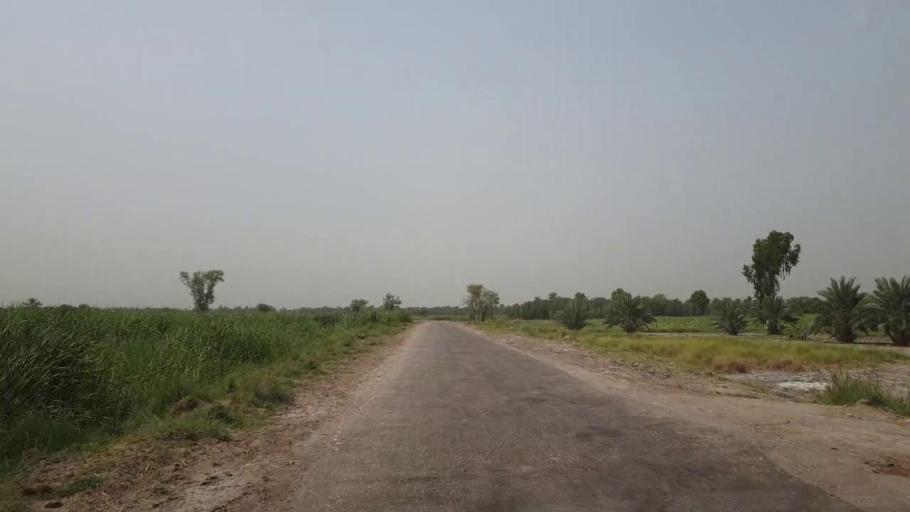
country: PK
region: Sindh
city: Gambat
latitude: 27.3880
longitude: 68.5491
